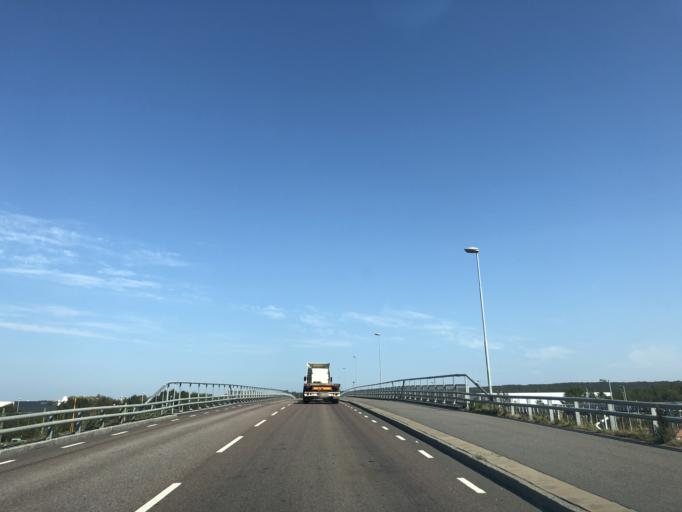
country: SE
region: Vaestra Goetaland
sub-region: Goteborg
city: Majorna
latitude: 57.6978
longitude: 11.8605
